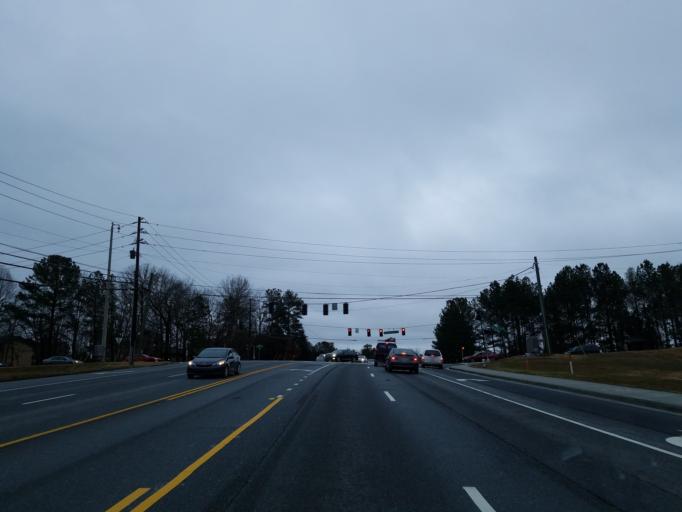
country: US
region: Georgia
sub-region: Gwinnett County
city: Norcross
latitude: 33.9595
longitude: -84.2473
